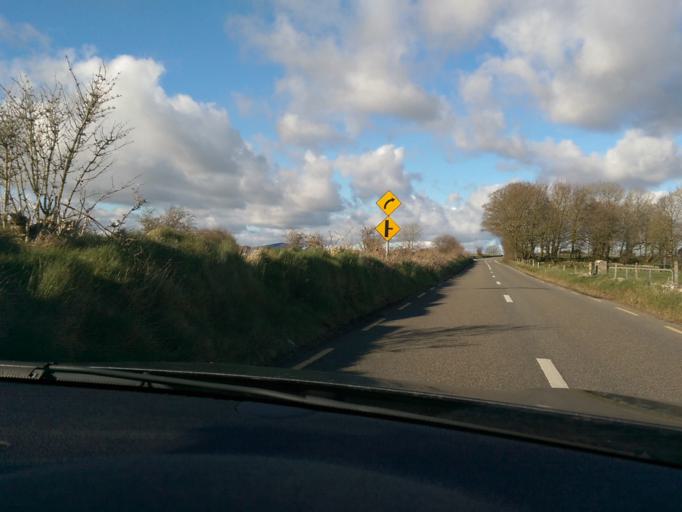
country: IE
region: Connaught
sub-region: Roscommon
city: Castlerea
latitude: 53.5722
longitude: -8.5665
